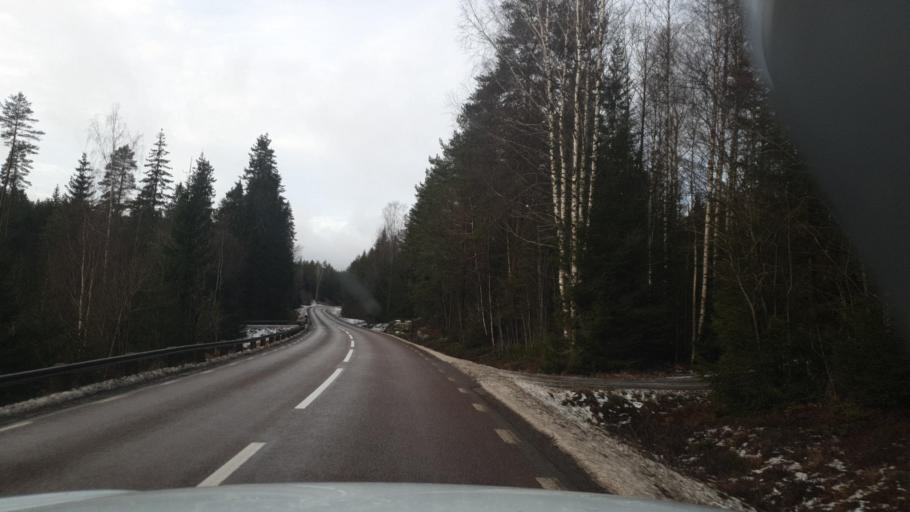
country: SE
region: Vaermland
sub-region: Eda Kommun
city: Amotfors
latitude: 59.7276
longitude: 12.2456
